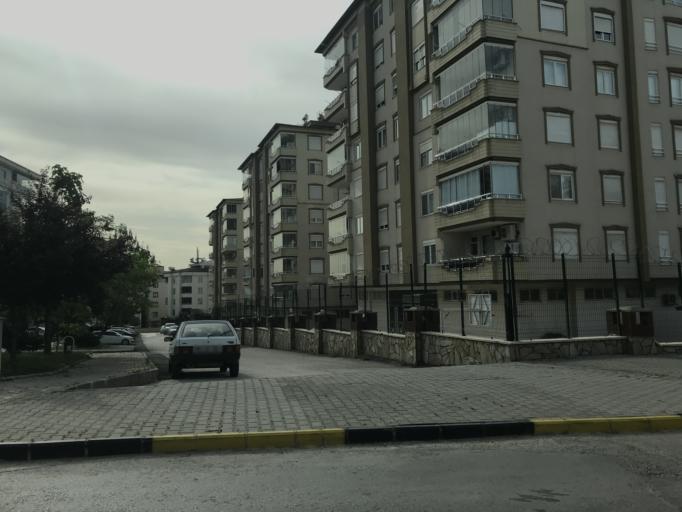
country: TR
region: Gaziantep
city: Sehitkamil
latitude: 37.0826
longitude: 37.3462
